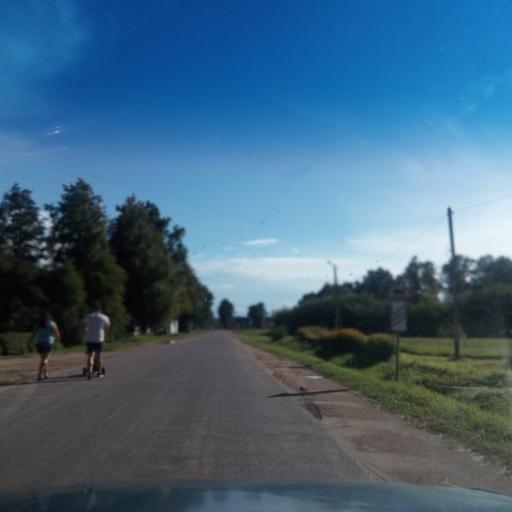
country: BY
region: Vitebsk
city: Dzisna
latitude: 55.6706
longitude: 28.3305
